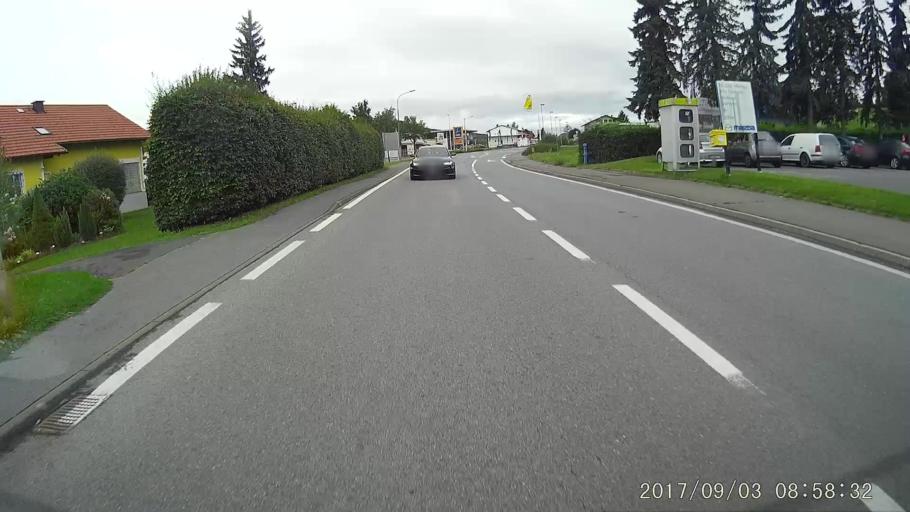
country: AT
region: Styria
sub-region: Politischer Bezirk Suedoststeiermark
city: Bad Gleichenberg
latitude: 46.8687
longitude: 15.9025
